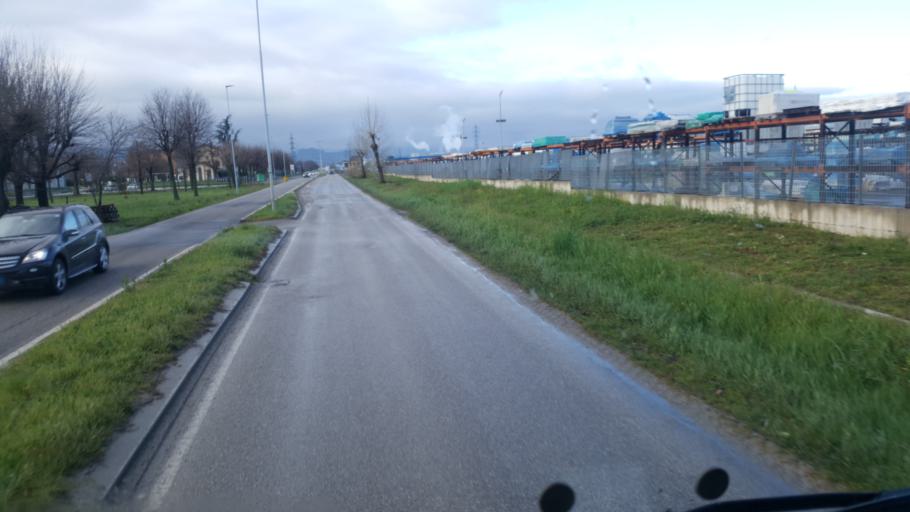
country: IT
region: Emilia-Romagna
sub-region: Provincia di Modena
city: Sassuolo
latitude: 44.5628
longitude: 10.7908
